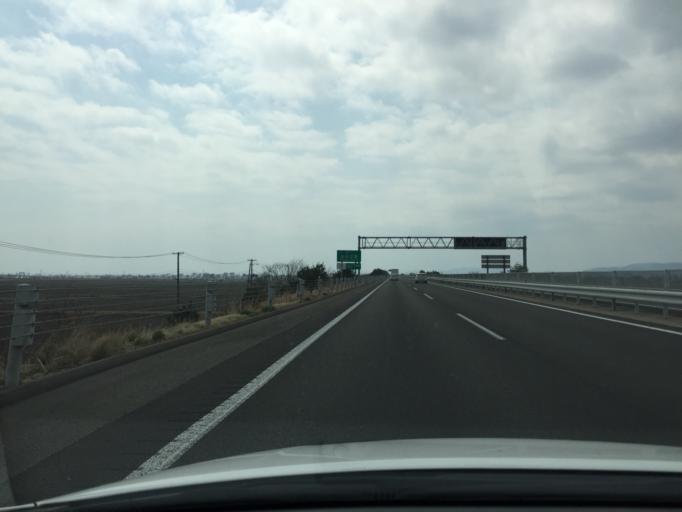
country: JP
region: Miyagi
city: Iwanuma
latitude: 38.1461
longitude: 140.8928
